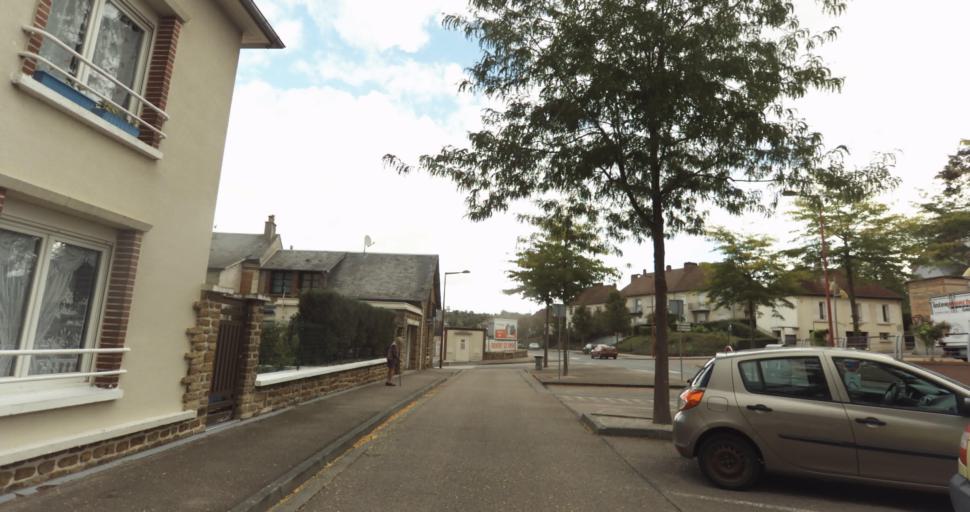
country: FR
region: Lower Normandy
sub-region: Departement de l'Orne
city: Gace
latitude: 48.7947
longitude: 0.2982
